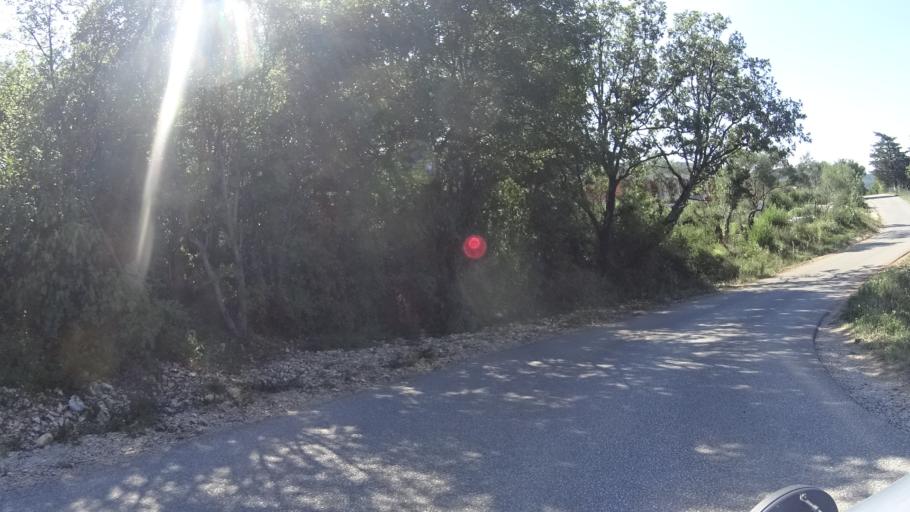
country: HR
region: Istarska
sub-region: Grad Labin
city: Rabac
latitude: 45.0091
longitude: 14.1595
